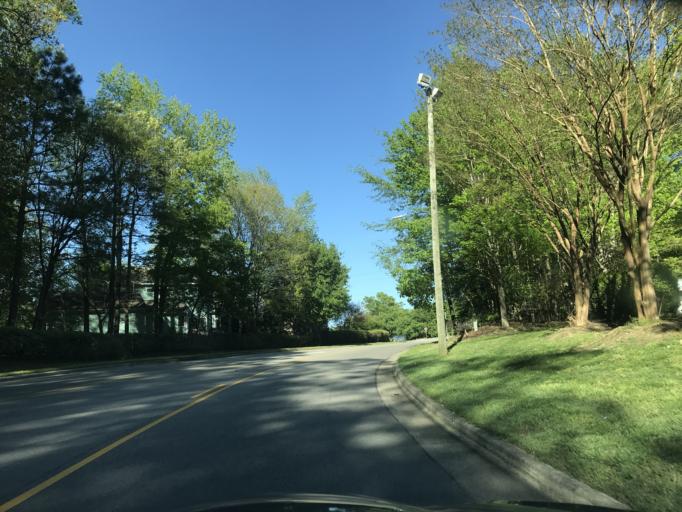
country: US
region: North Carolina
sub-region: Wake County
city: Knightdale
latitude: 35.8036
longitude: -78.5565
